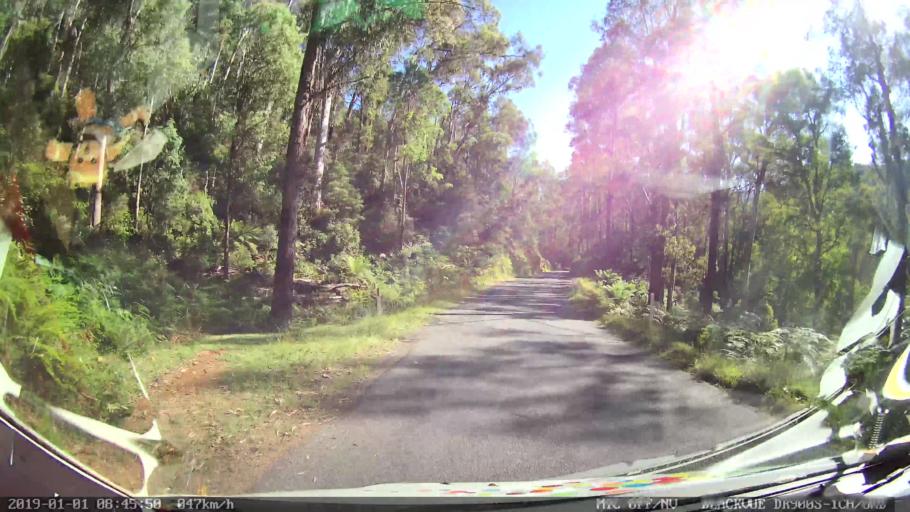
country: AU
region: New South Wales
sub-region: Snowy River
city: Jindabyne
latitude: -36.3031
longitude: 148.1903
